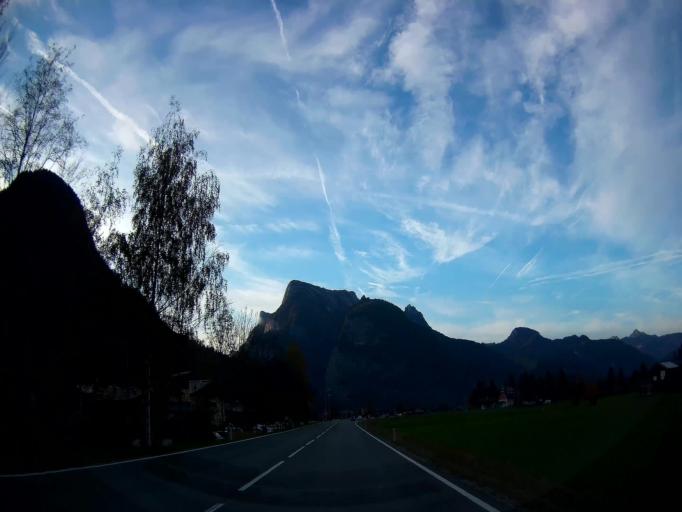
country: AT
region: Salzburg
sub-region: Politischer Bezirk Zell am See
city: Sankt Martin bei Lofer
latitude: 47.5678
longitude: 12.7060
